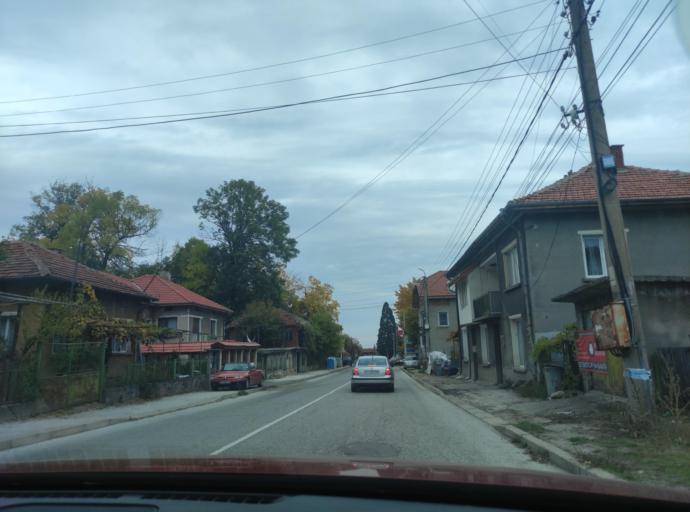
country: BG
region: Montana
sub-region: Obshtina Berkovitsa
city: Berkovitsa
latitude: 43.1971
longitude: 23.1609
